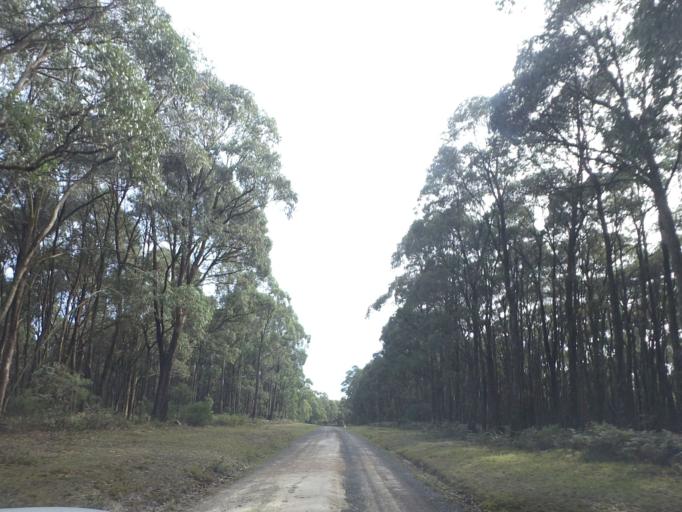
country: AU
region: Victoria
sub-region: Moorabool
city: Bacchus Marsh
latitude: -37.4727
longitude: 144.2136
